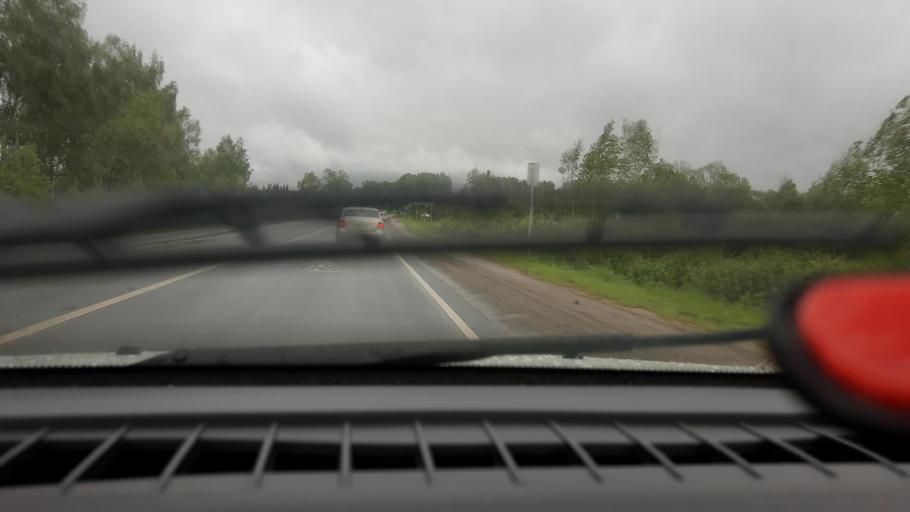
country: RU
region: Nizjnij Novgorod
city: Linda
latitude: 56.6154
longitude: 44.0648
